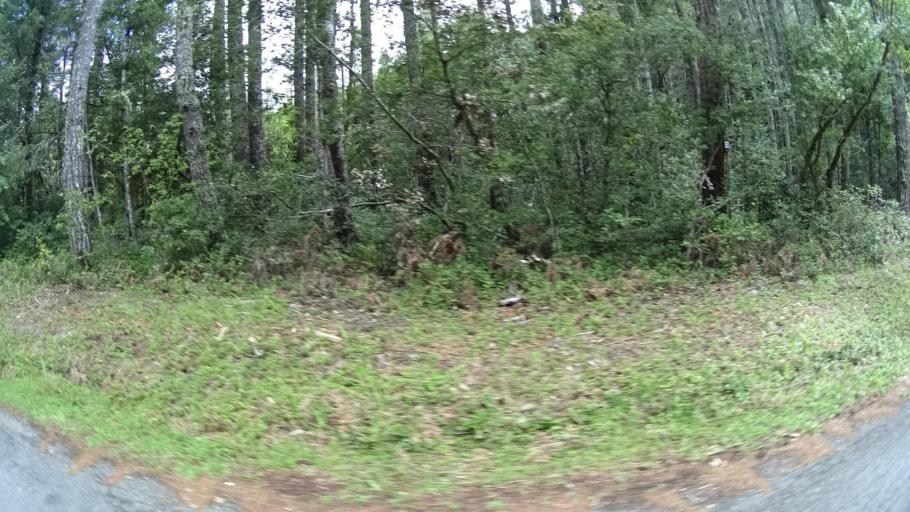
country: US
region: California
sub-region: Humboldt County
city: Blue Lake
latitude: 40.7955
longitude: -123.9795
